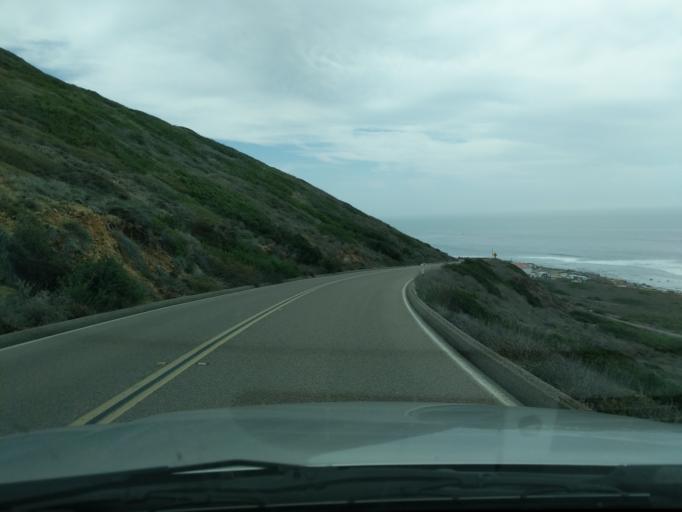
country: US
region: California
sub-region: San Diego County
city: Coronado
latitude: 32.6715
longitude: -117.2428
